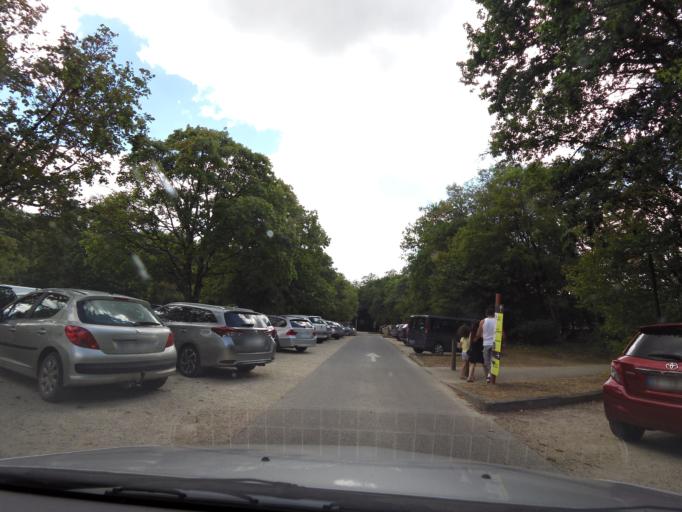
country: FR
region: Poitou-Charentes
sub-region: Departement des Deux-Sevres
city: Beauvoir-sur-Niort
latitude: 46.1441
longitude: -0.3947
